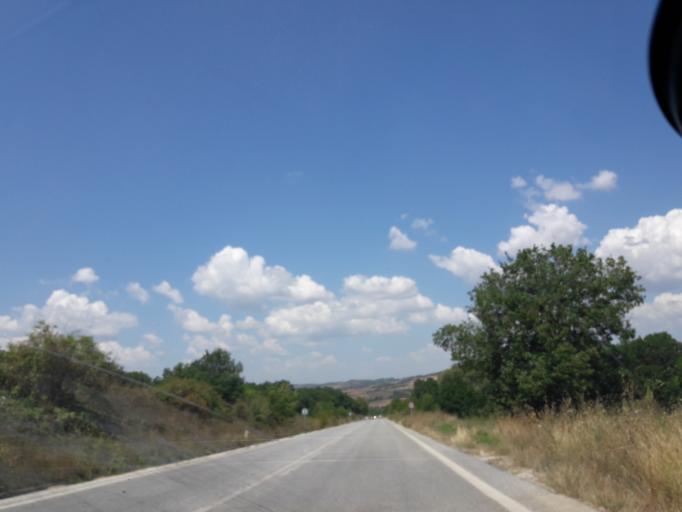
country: GR
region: Central Macedonia
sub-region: Nomos Chalkidikis
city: Polygyros
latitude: 40.4566
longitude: 23.4049
